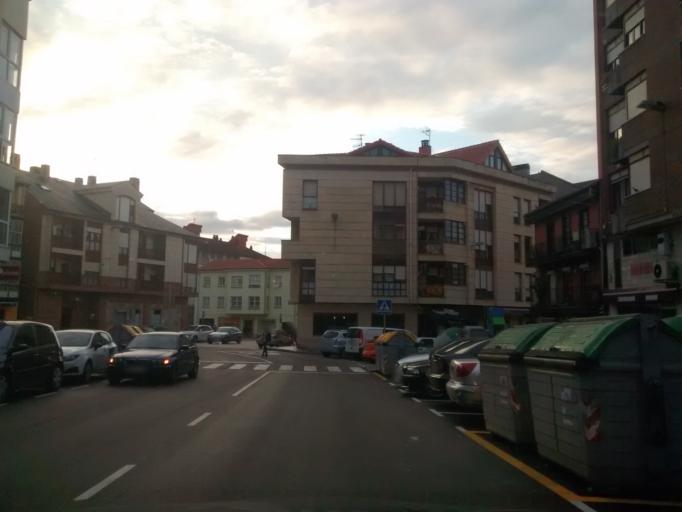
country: ES
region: Cantabria
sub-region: Provincia de Cantabria
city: Torrelavega
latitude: 43.3469
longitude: -4.0468
